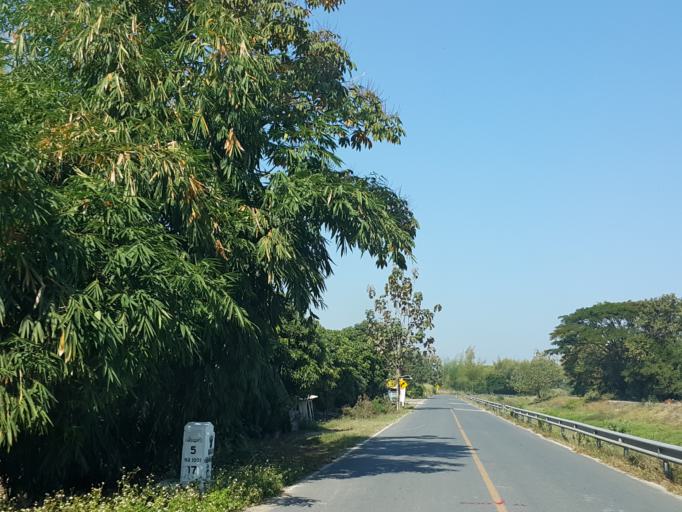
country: TH
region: Chiang Mai
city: San Sai
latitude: 18.9369
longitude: 98.9964
